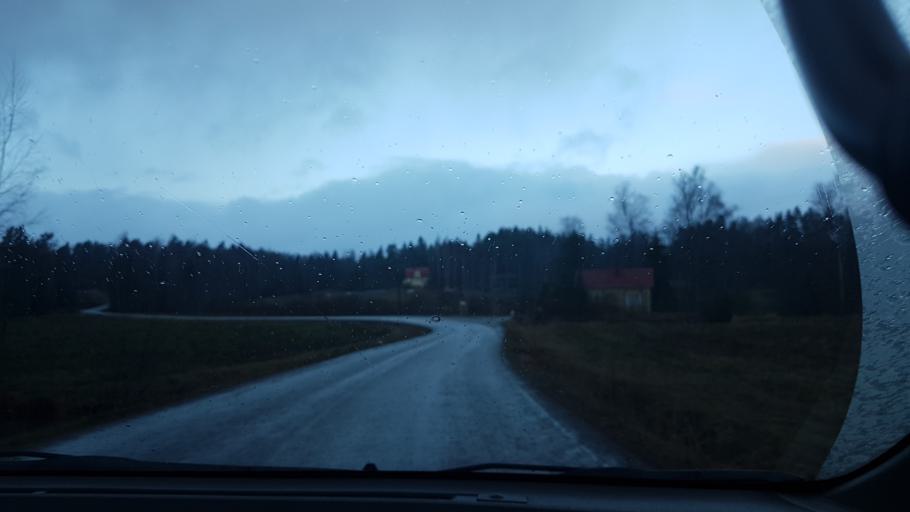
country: FI
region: Uusimaa
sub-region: Helsinki
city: Lohja
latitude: 60.2133
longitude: 24.0993
